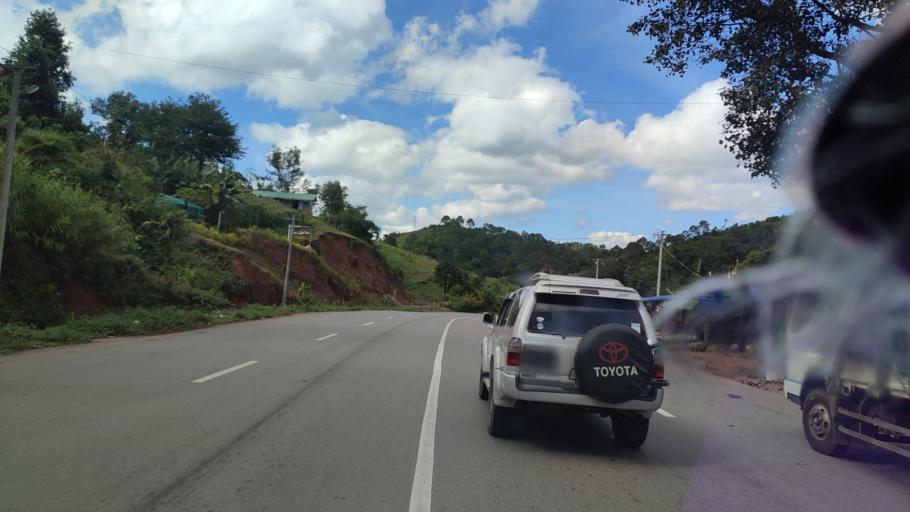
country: MM
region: Mandalay
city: Yamethin
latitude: 20.6570
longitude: 96.5433
